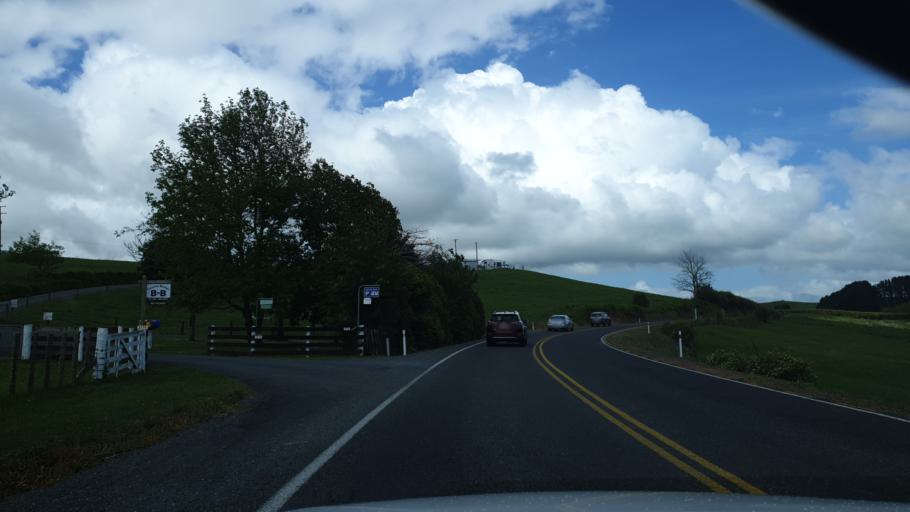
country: NZ
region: Waikato
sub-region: Matamata-Piako District
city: Matamata
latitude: -37.8798
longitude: 175.6978
